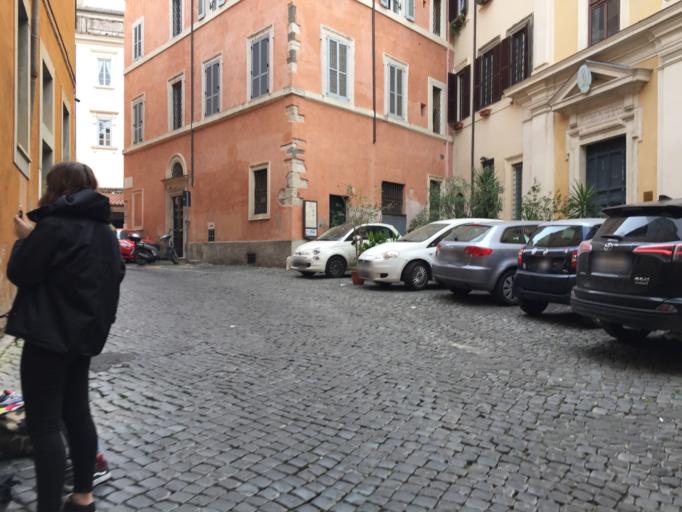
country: VA
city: Vatican City
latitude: 41.8973
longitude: 12.4794
